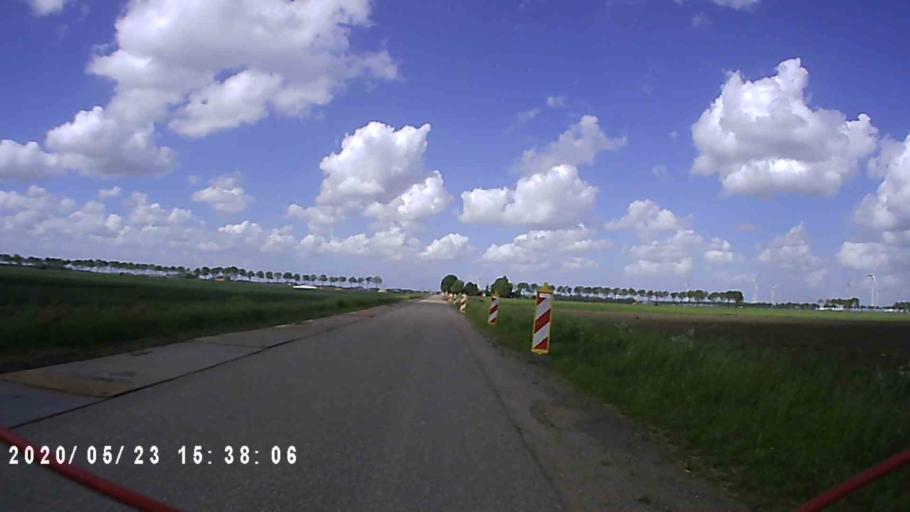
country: NL
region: Groningen
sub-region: Gemeente Delfzijl
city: Delfzijl
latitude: 53.2762
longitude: 6.9407
